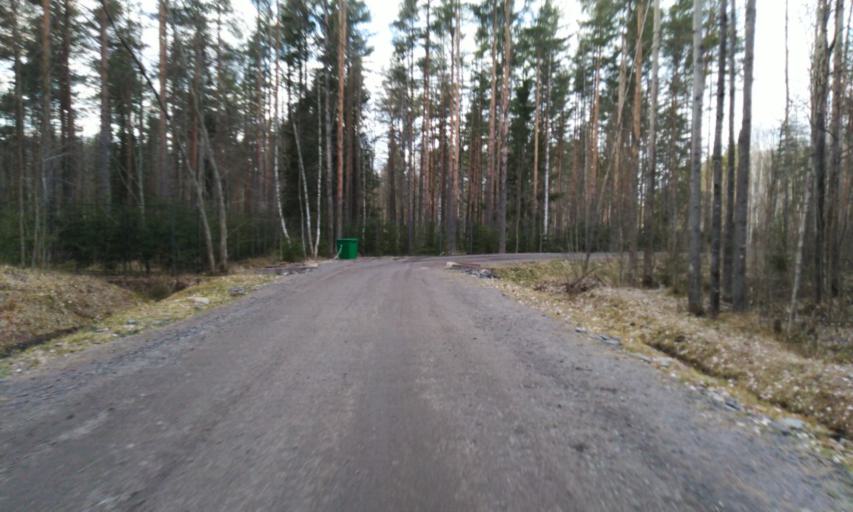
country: RU
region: Leningrad
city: Toksovo
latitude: 60.1196
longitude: 30.4790
